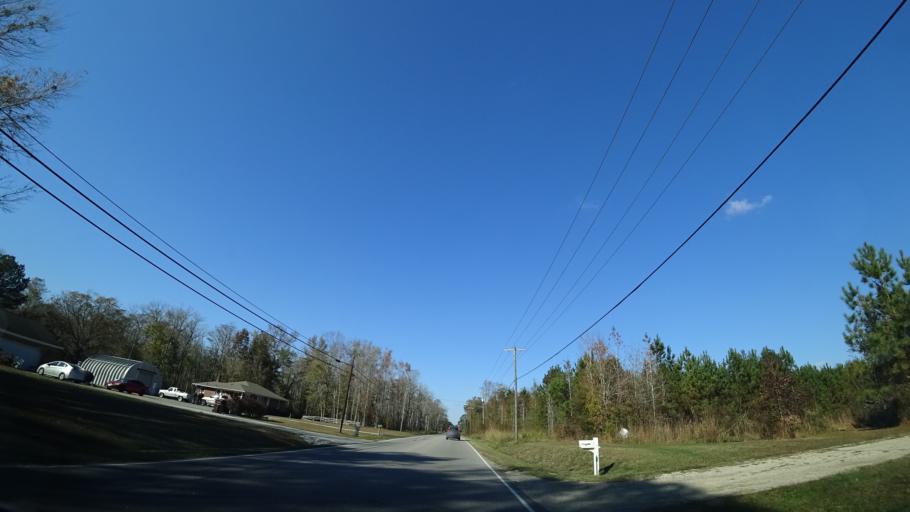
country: US
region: North Carolina
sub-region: Currituck County
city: Moyock
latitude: 36.5828
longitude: -76.2034
